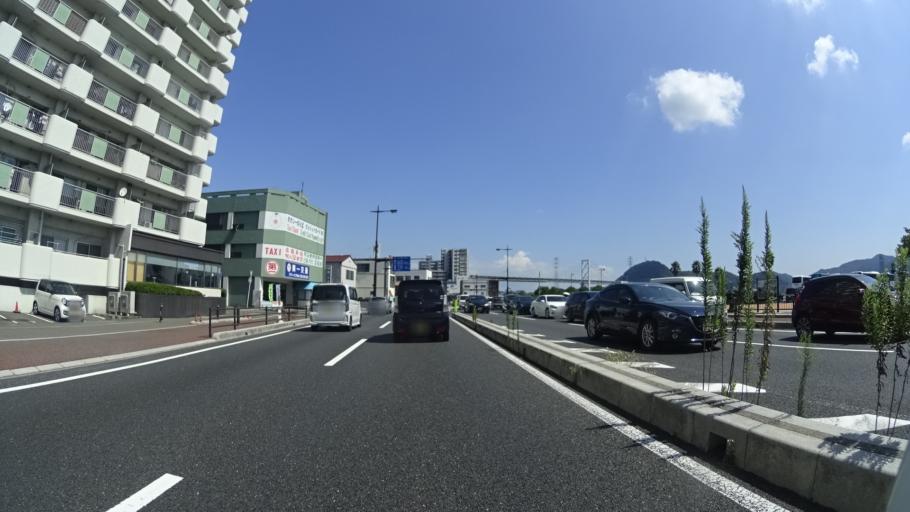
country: JP
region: Yamaguchi
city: Shimonoseki
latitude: 33.9577
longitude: 130.9465
